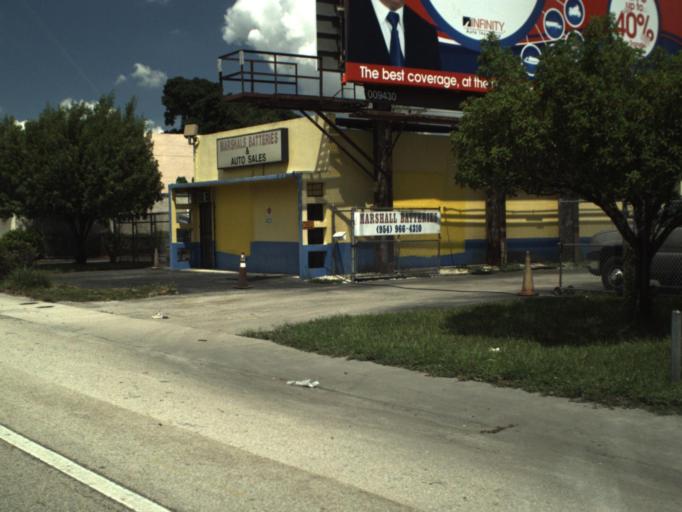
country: US
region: Florida
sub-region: Broward County
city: Lake Forest
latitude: 25.9845
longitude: -80.1853
